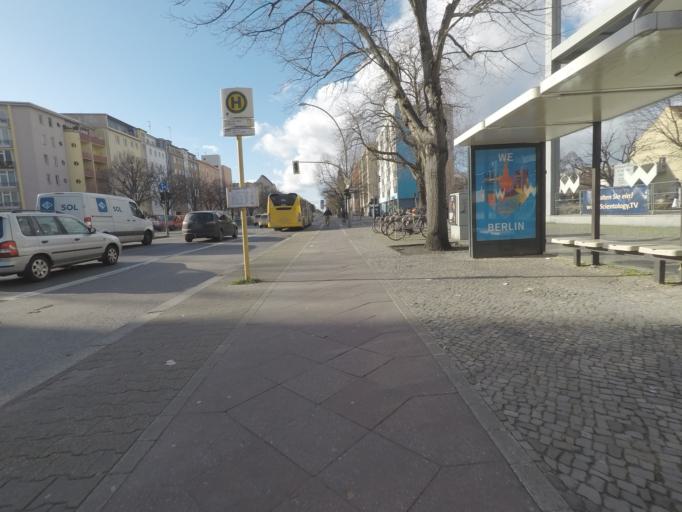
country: DE
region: Berlin
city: Moabit
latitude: 52.5146
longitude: 13.3159
